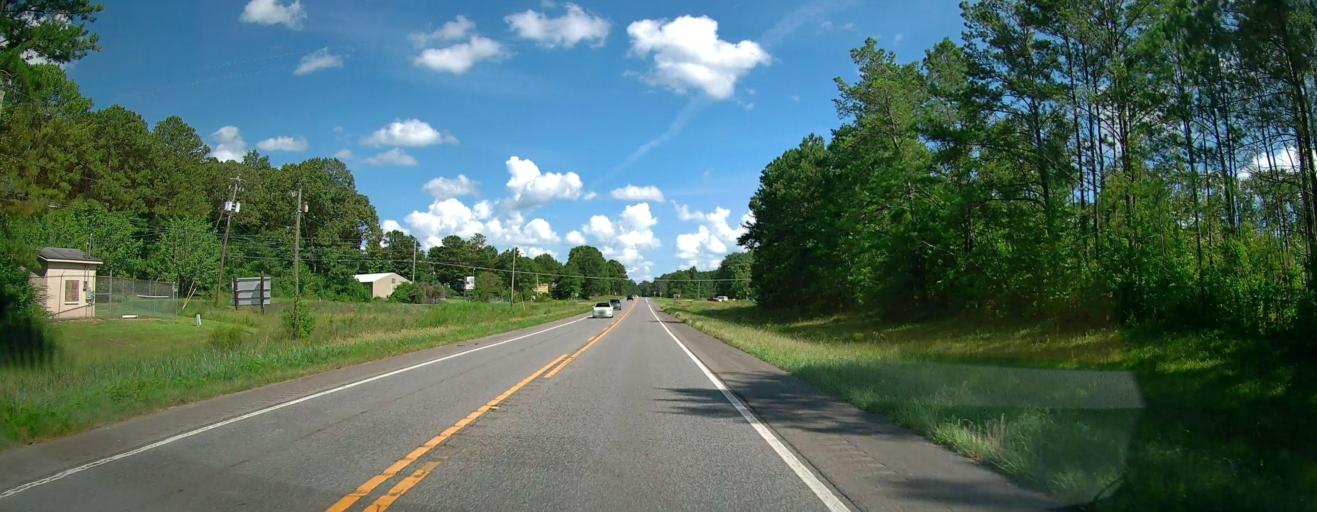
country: US
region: Alabama
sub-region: Pickens County
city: Gordo
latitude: 33.3002
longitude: -87.8804
